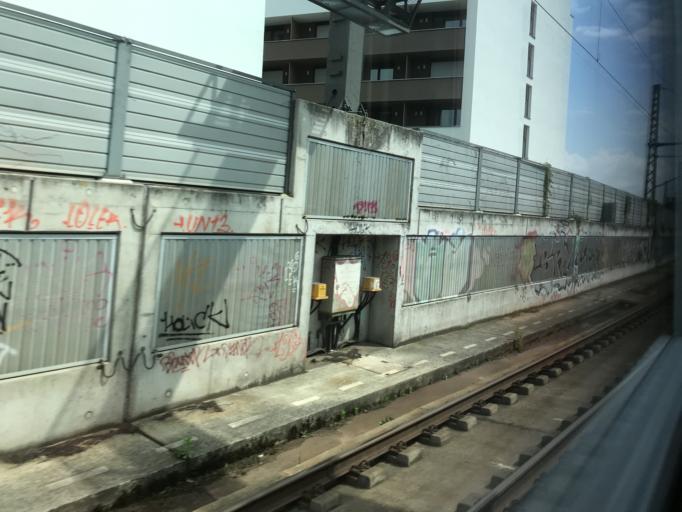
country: DE
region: Baden-Wuerttemberg
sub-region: Tuebingen Region
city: Ulm
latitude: 48.3903
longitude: 9.9959
